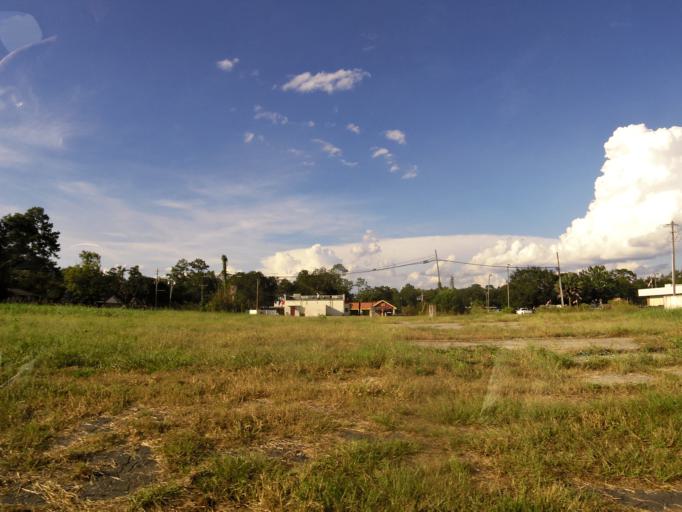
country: US
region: Georgia
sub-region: Brooks County
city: Quitman
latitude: 30.7832
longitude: -83.5542
